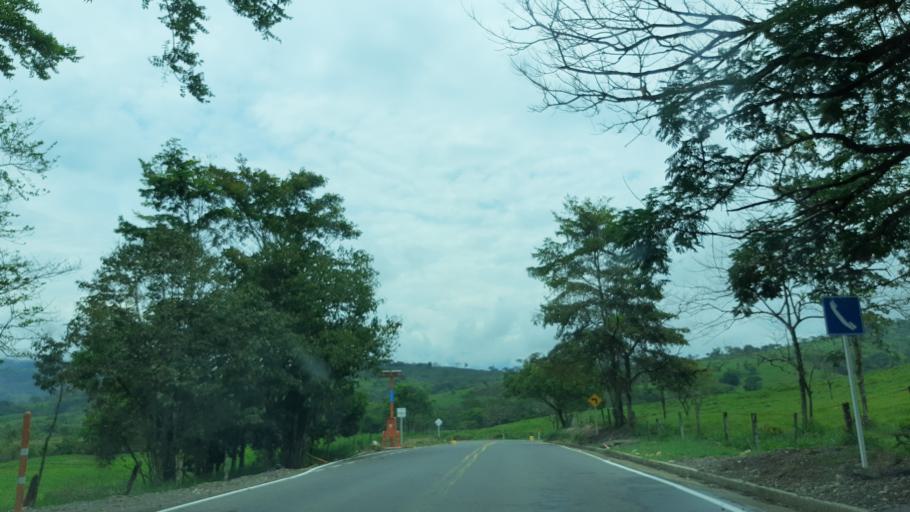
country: CO
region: Casanare
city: Sabanalarga
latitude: 4.8099
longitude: -73.0588
